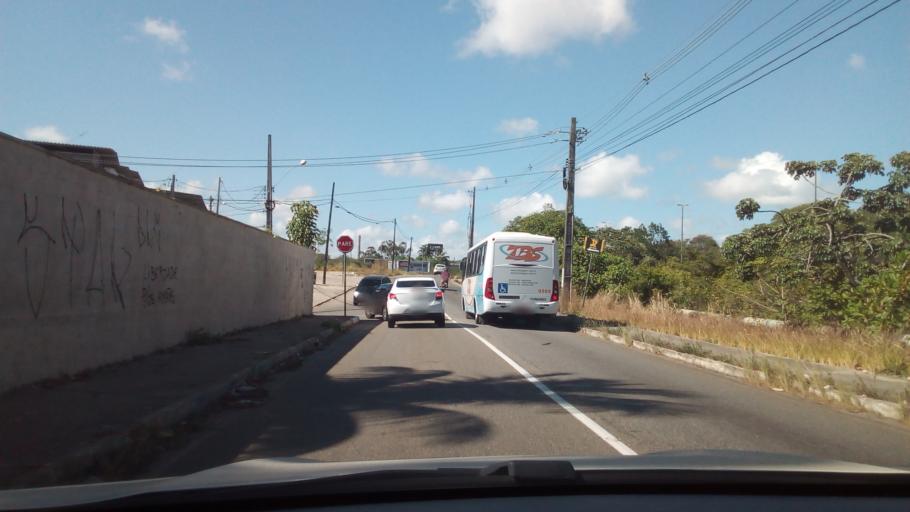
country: BR
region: Paraiba
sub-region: Joao Pessoa
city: Joao Pessoa
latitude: -7.1550
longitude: -34.8560
